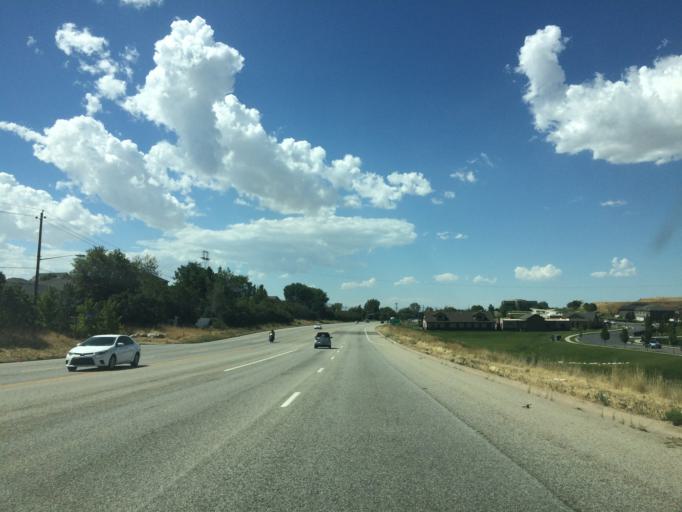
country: US
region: Utah
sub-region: Davis County
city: South Weber
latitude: 41.1037
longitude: -111.9276
